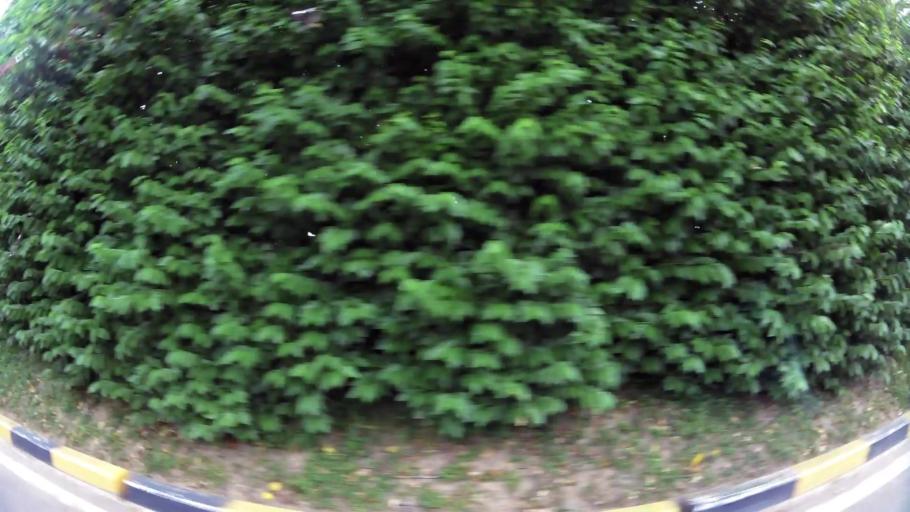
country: SG
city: Singapore
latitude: 1.3397
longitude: 103.7964
